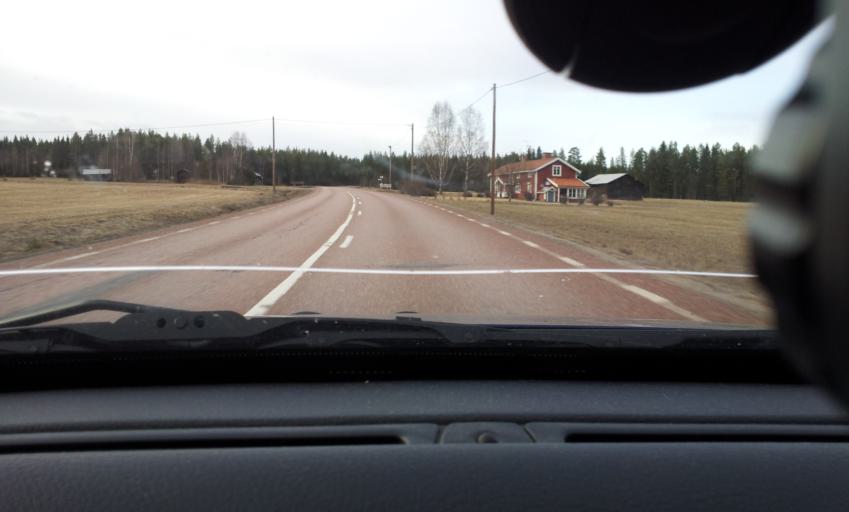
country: SE
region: Gaevleborg
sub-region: Ljusdals Kommun
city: Farila
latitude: 61.8377
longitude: 15.7517
